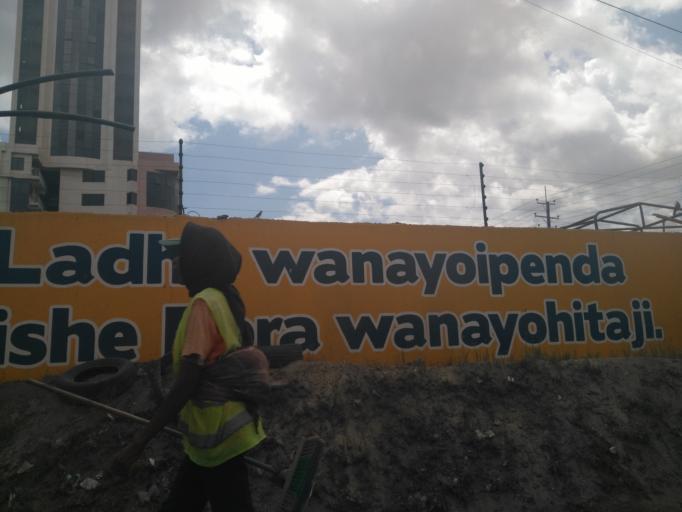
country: TZ
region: Dar es Salaam
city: Dar es Salaam
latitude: -6.8269
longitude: 39.2612
